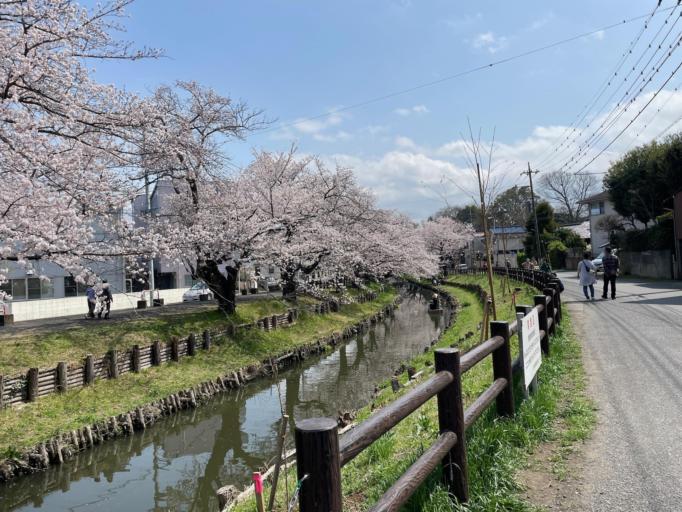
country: JP
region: Saitama
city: Kawagoe
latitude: 35.9290
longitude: 139.4869
